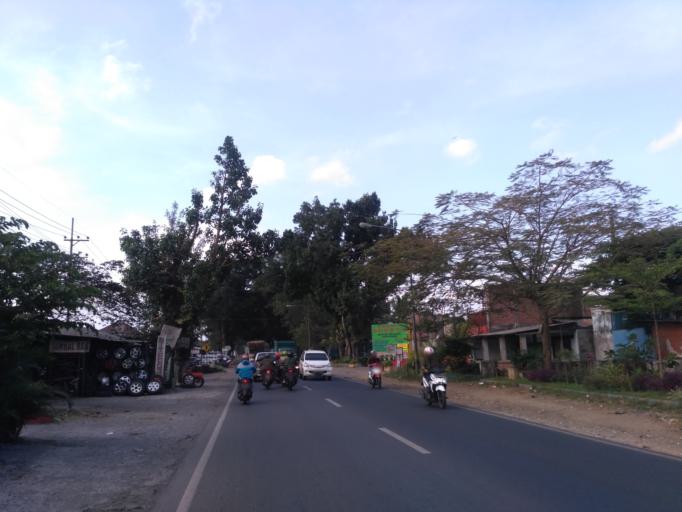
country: ID
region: East Java
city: Watudakon
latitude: -8.0378
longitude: 112.6107
